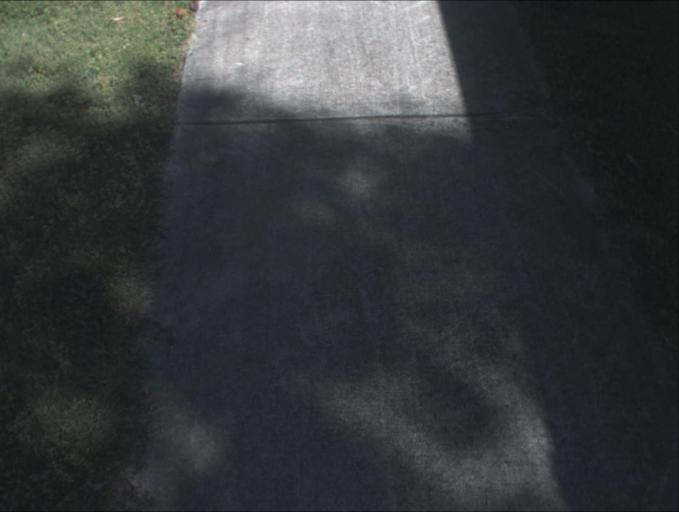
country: AU
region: Queensland
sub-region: Logan
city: Park Ridge South
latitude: -27.7380
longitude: 153.0287
